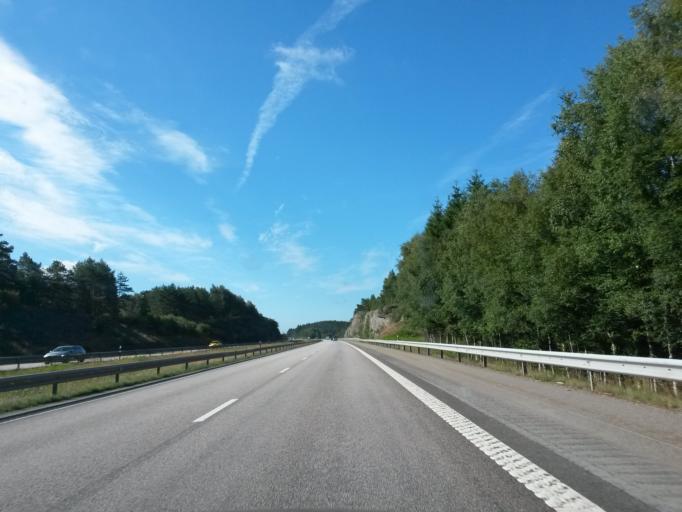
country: SE
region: Halland
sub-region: Kungsbacka Kommun
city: Frillesas
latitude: 57.3454
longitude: 12.2078
